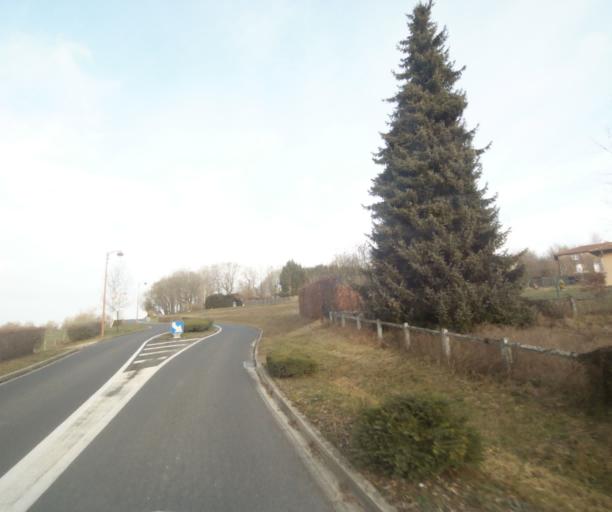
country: FR
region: Champagne-Ardenne
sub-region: Departement de la Marne
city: Sermaize-les-Bains
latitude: 48.7230
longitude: 4.9412
